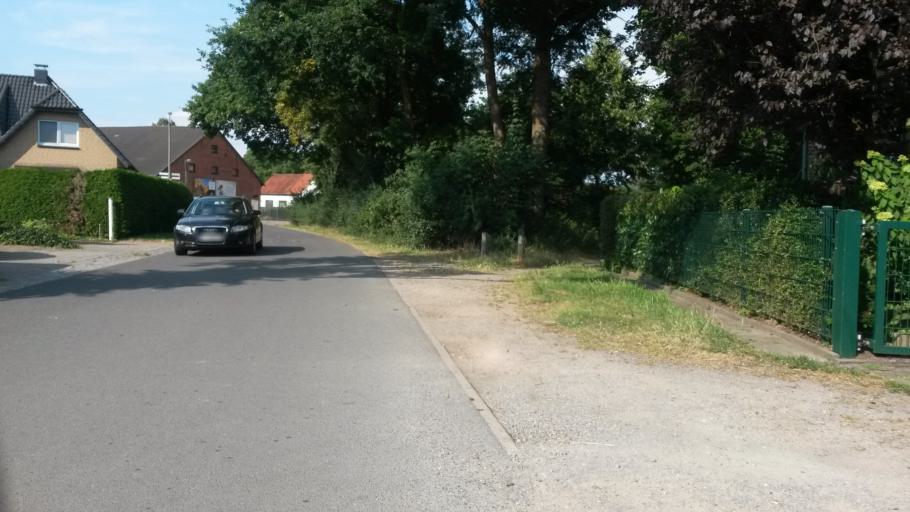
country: DE
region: Lower Saxony
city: Riede
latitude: 53.0378
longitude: 8.9390
